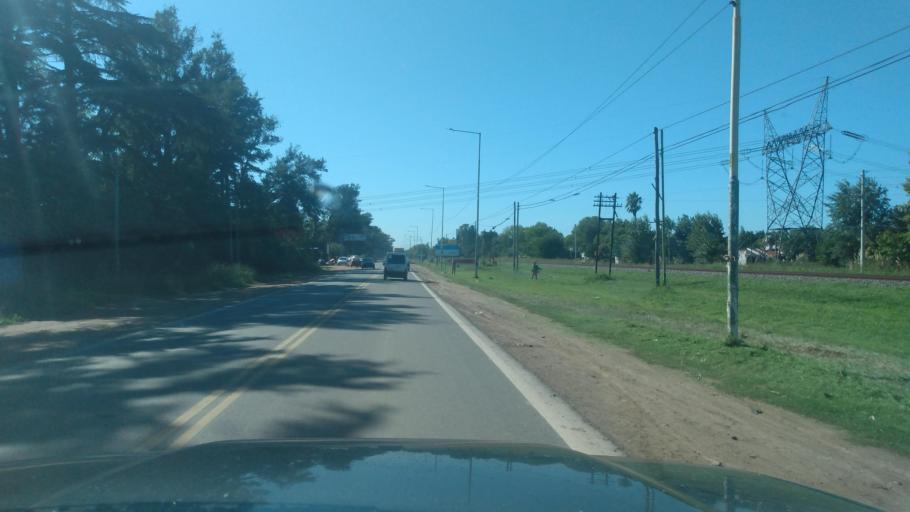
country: AR
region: Buenos Aires
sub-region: Partido de General Rodriguez
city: General Rodriguez
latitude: -34.6012
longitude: -58.9850
